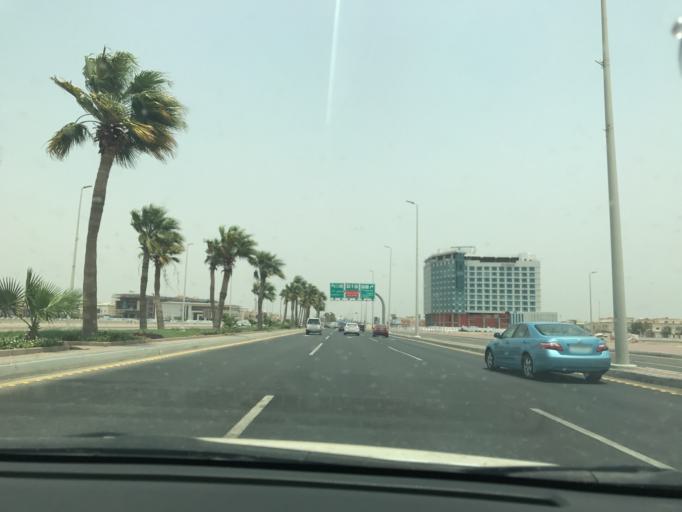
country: SA
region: Makkah
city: Jeddah
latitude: 21.6673
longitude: 39.1184
